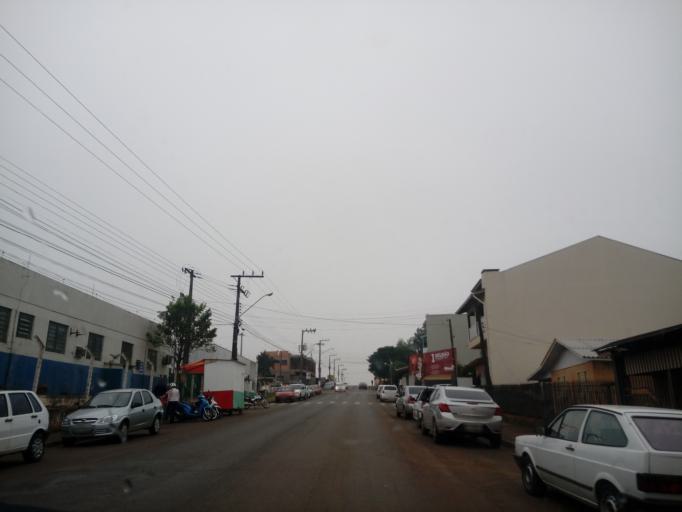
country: BR
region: Santa Catarina
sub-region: Chapeco
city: Chapeco
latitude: -27.1011
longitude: -52.6736
